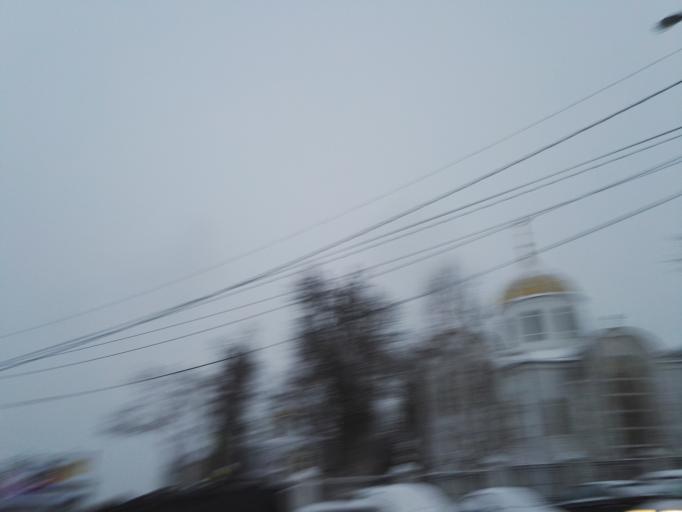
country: RU
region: Tula
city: Mendeleyevskiy
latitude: 54.1684
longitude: 37.5909
